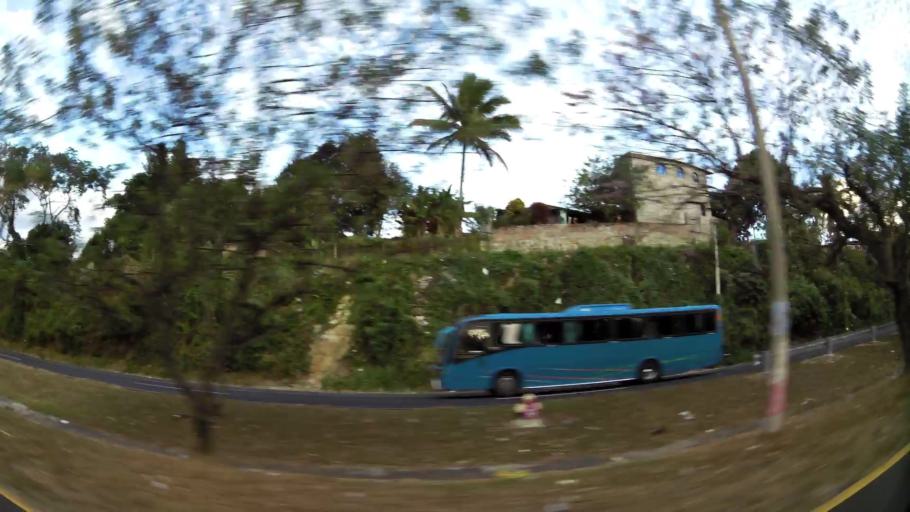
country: SV
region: San Vicente
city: San Sebastian
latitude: 13.6758
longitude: -88.8448
